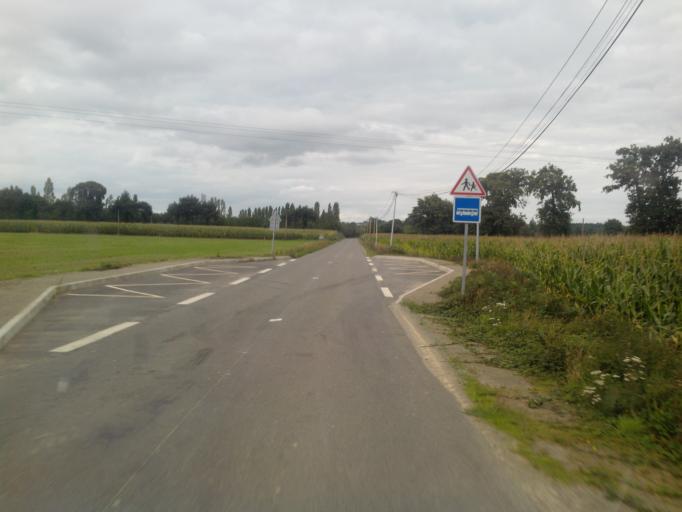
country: FR
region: Brittany
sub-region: Departement d'Ille-et-Vilaine
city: Melesse
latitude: 48.2374
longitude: -1.6763
